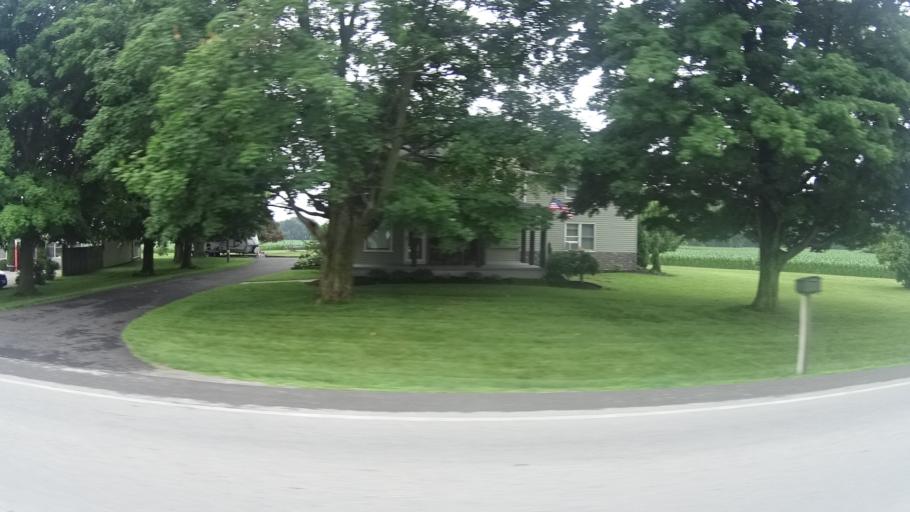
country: US
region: Ohio
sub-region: Erie County
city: Milan
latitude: 41.3171
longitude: -82.6002
